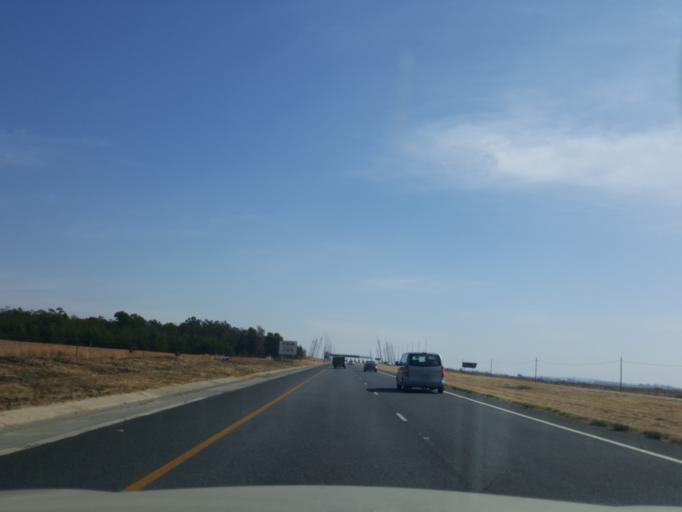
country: ZA
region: Gauteng
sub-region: City of Tshwane Metropolitan Municipality
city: Cullinan
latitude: -25.7982
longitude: 28.5600
